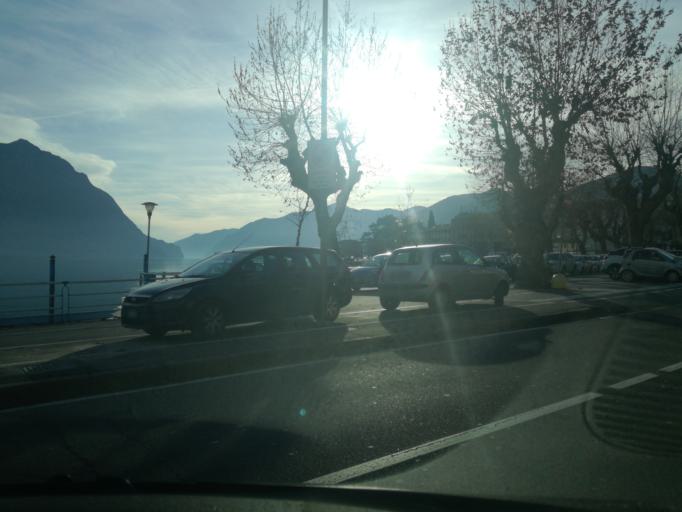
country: IT
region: Lombardy
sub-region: Provincia di Bergamo
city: Lovere
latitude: 45.8218
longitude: 10.0811
